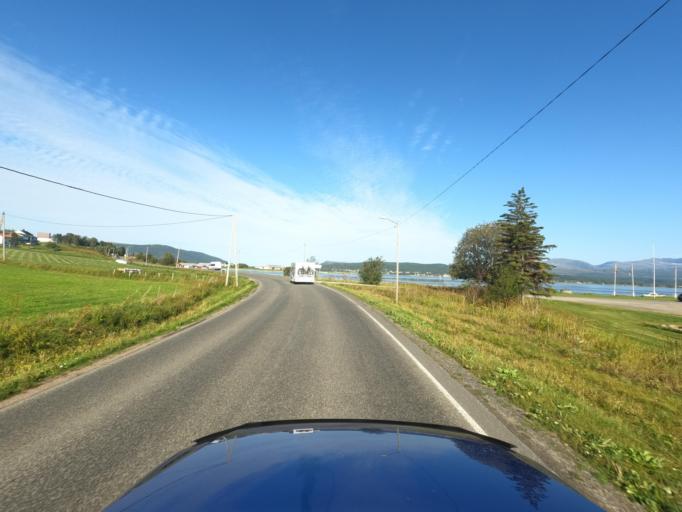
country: NO
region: Troms
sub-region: Skanland
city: Evenskjer
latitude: 68.5692
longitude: 16.5145
